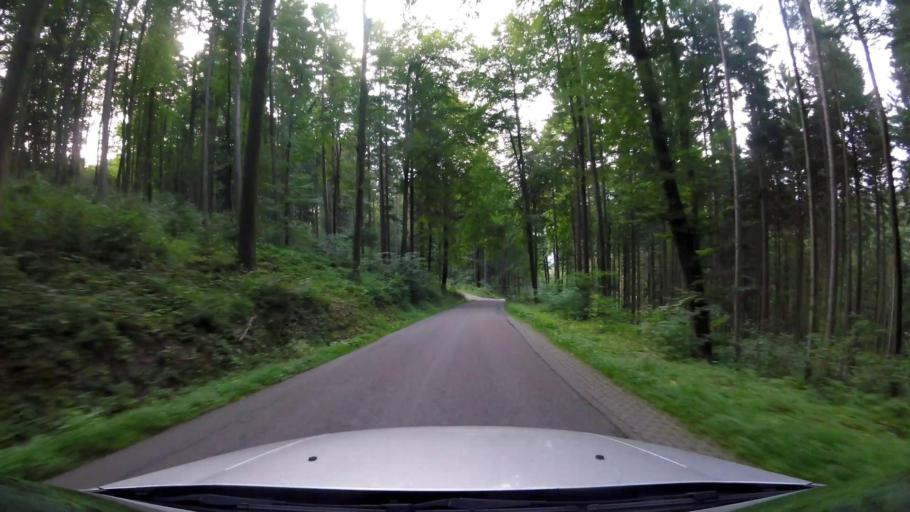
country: DE
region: Baden-Wuerttemberg
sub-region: Regierungsbezirk Stuttgart
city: Urbach
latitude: 48.8564
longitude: 9.5731
